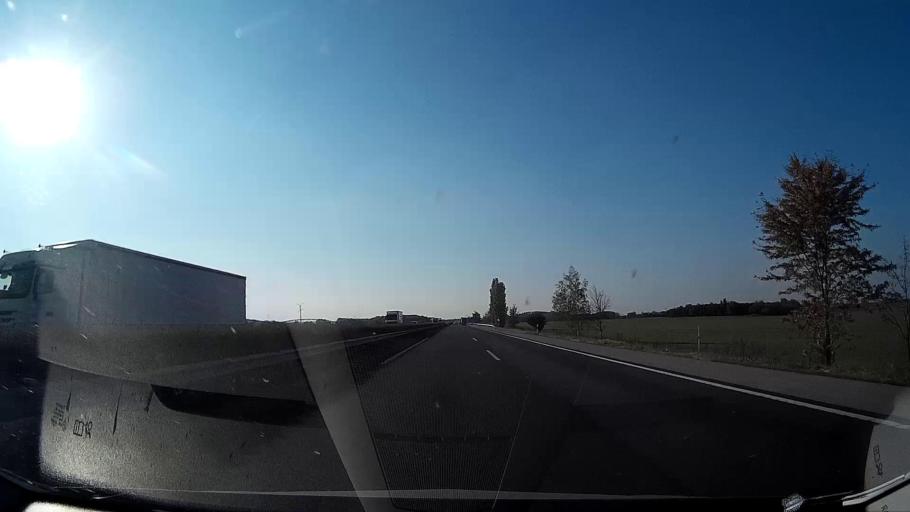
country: HU
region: Gyor-Moson-Sopron
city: Bony
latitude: 47.6812
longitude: 17.9091
